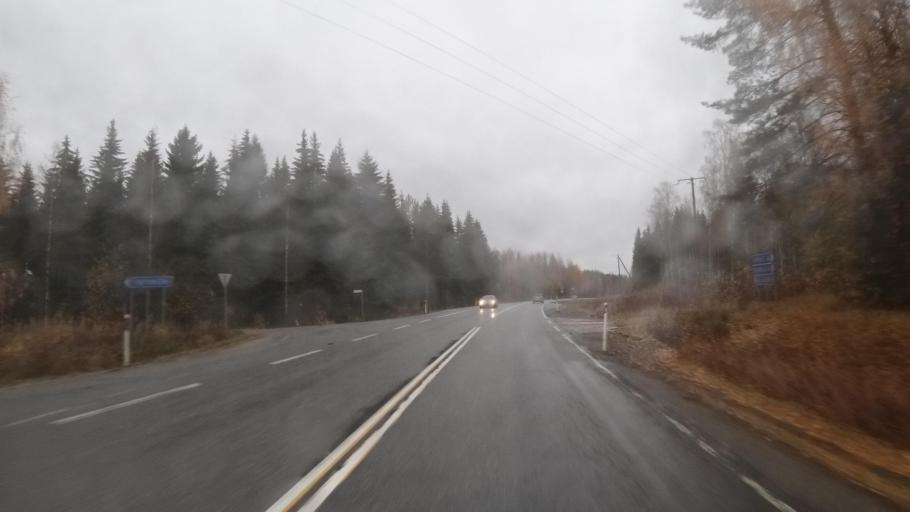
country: FI
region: North Karelia
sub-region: Joensuu
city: Outokumpu
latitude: 62.5354
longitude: 28.9007
